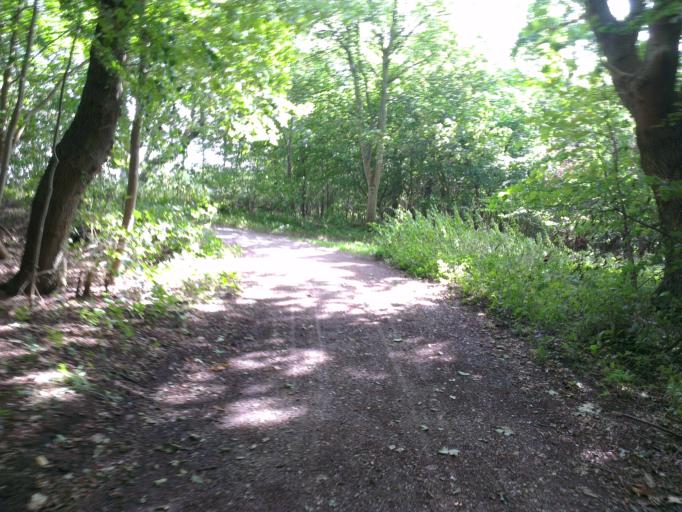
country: DK
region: Capital Region
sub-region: Frederikssund Kommune
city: Jaegerspris
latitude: 55.8531
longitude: 11.9617
